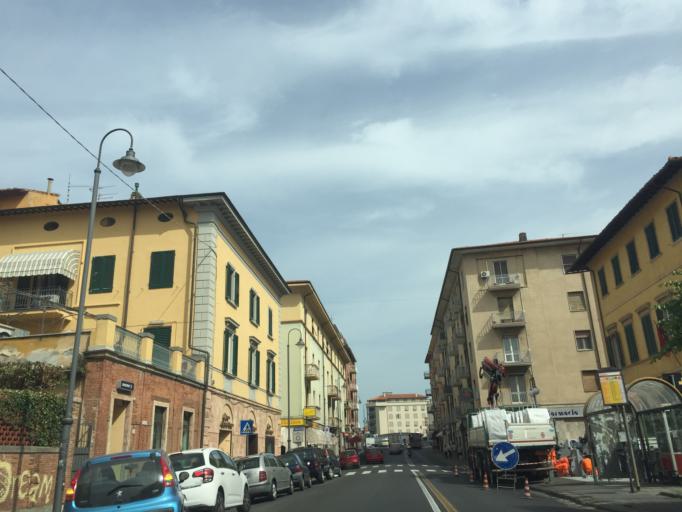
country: IT
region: Tuscany
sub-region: Province of Pisa
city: Pisa
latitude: 43.7134
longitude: 10.3963
